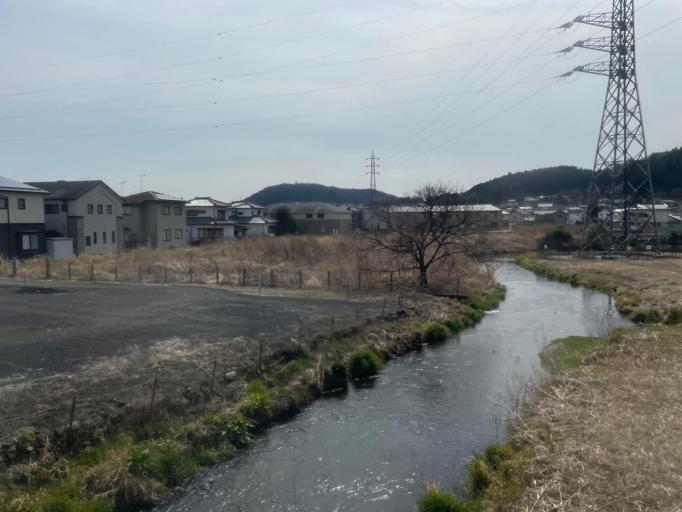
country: JP
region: Shizuoka
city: Fujinomiya
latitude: 35.2288
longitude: 138.5928
